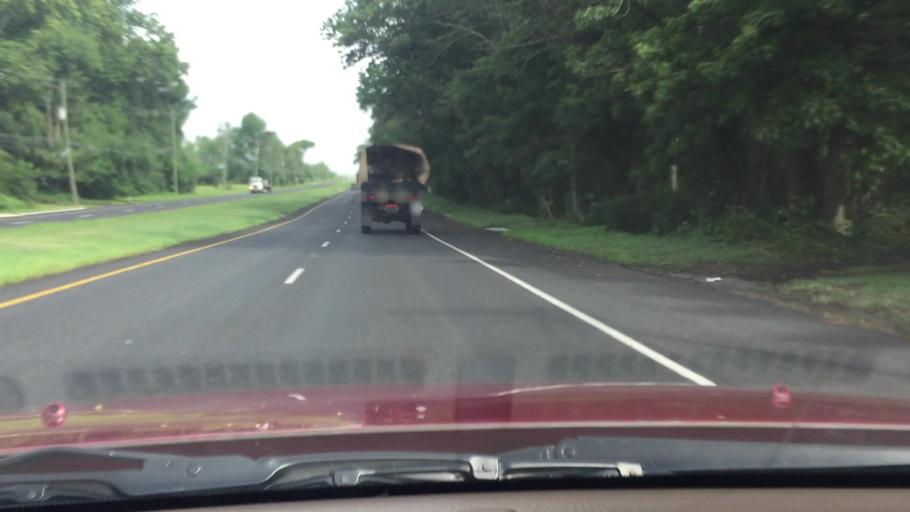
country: US
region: New Jersey
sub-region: Burlington County
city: Bordentown
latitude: 40.1000
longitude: -74.6888
